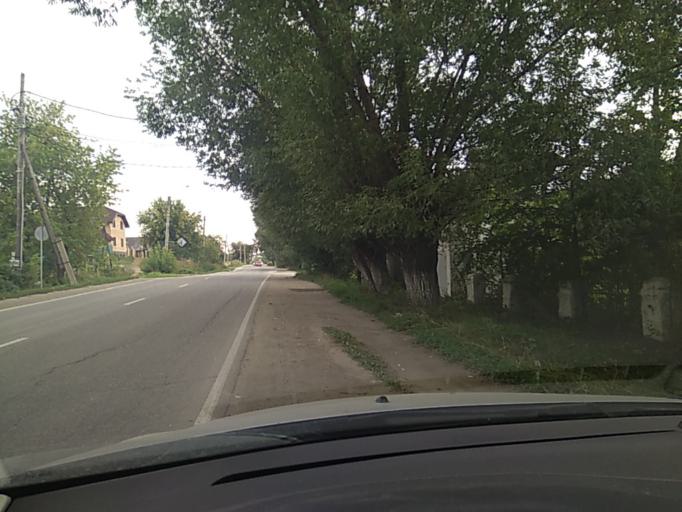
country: RU
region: Chelyabinsk
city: Kyshtym
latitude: 55.6990
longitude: 60.5525
